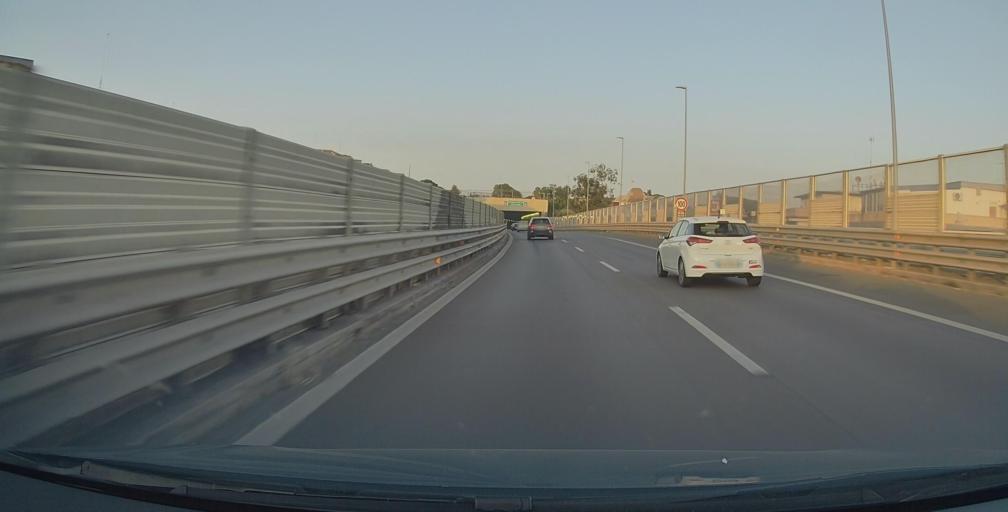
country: IT
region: Sicily
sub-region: Catania
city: Sant'Agata Li Battiati
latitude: 37.5496
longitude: 15.0723
